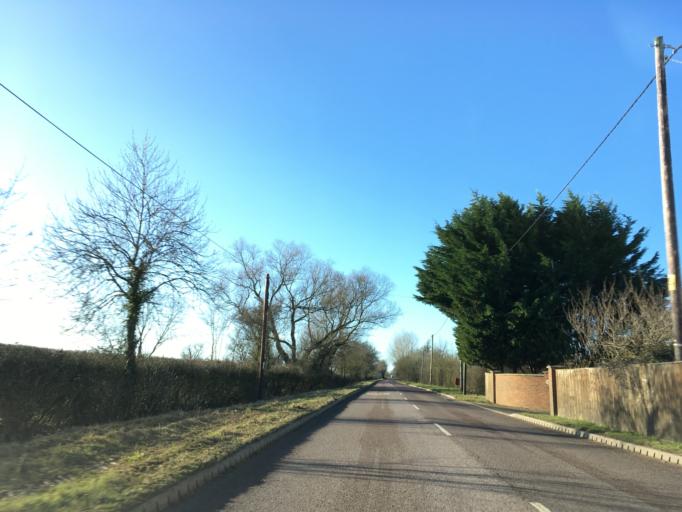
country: GB
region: England
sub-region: Wiltshire
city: Leigh
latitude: 51.6209
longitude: -1.9225
